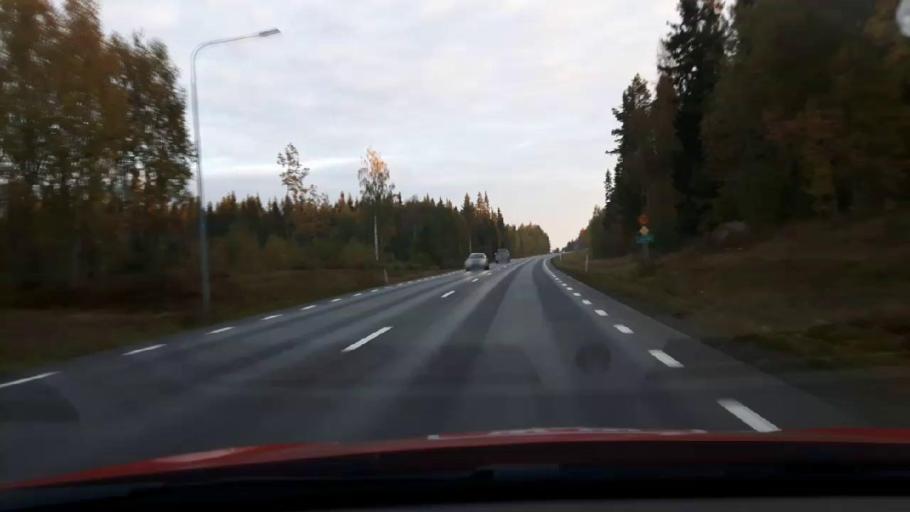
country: SE
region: Jaemtland
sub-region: OEstersunds Kommun
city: Lit
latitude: 63.3068
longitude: 14.8707
